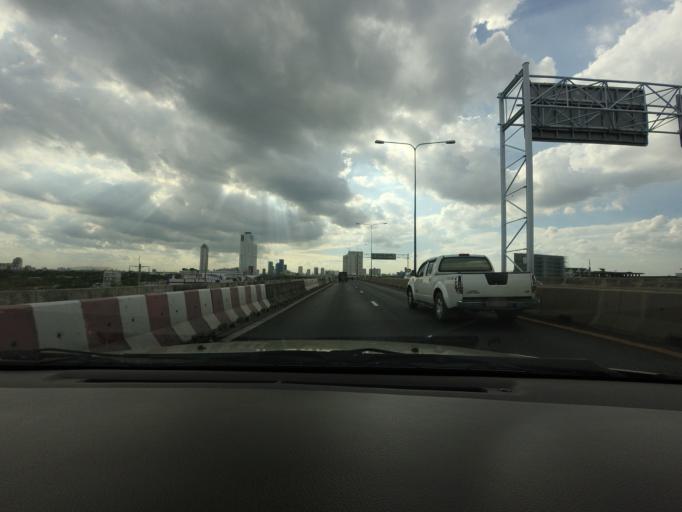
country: TH
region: Bangkok
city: Bang Na
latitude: 13.6621
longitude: 100.6603
